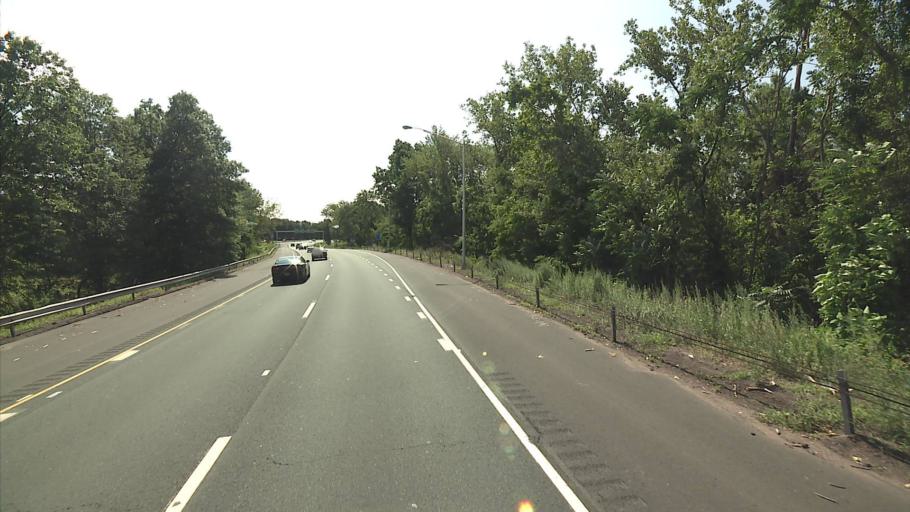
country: US
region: Connecticut
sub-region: Hartford County
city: Hartford
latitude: 41.7540
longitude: -72.6485
